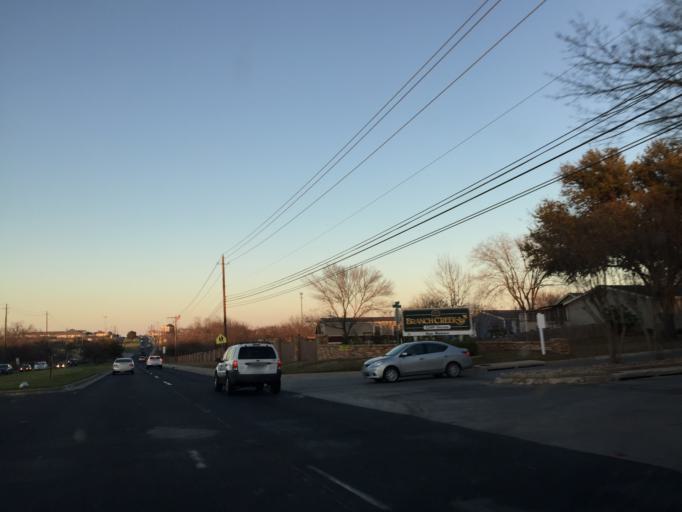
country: US
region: Texas
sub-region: Travis County
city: Pflugerville
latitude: 30.3943
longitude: -97.6444
